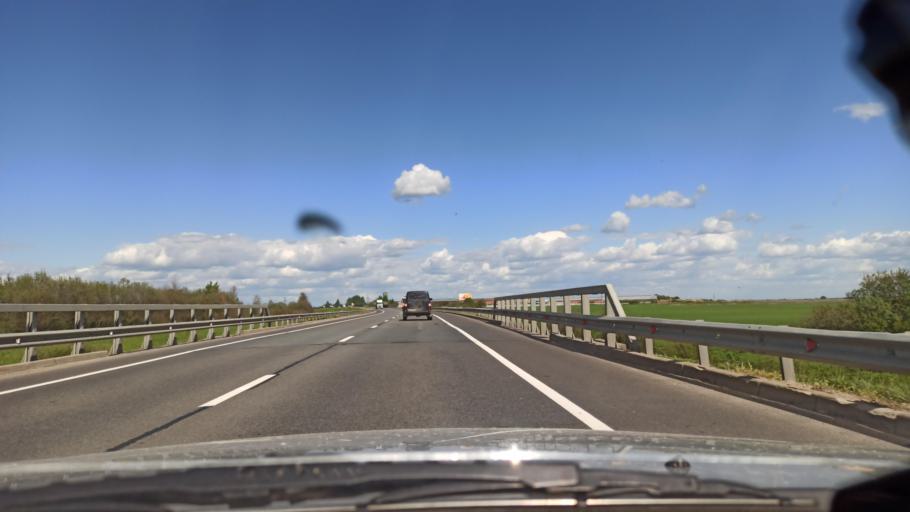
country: RU
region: Vologda
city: Vologda
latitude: 59.2782
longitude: 39.8277
